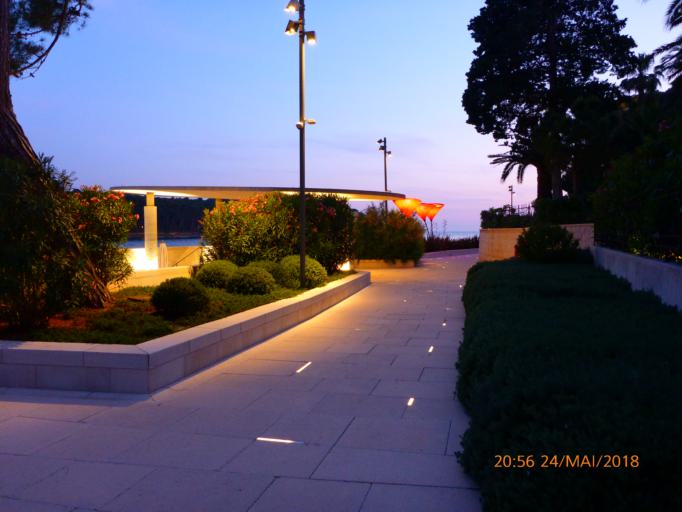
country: HR
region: Primorsko-Goranska
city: Mali Losinj
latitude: 44.5307
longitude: 14.4588
